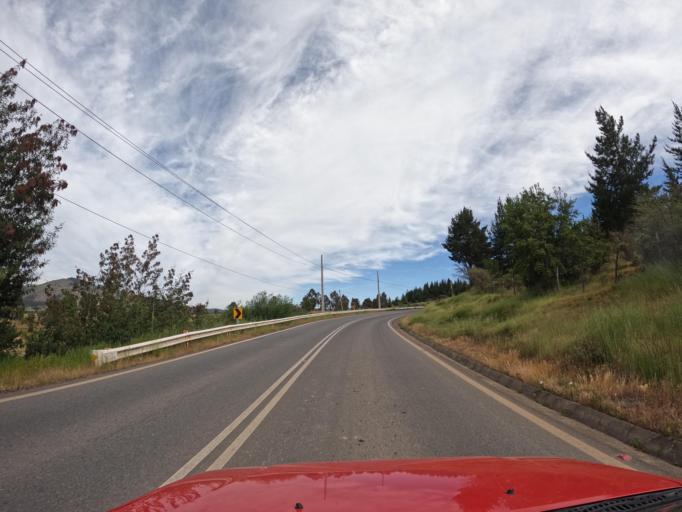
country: CL
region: Maule
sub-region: Provincia de Talca
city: Talca
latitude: -35.3252
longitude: -71.9301
